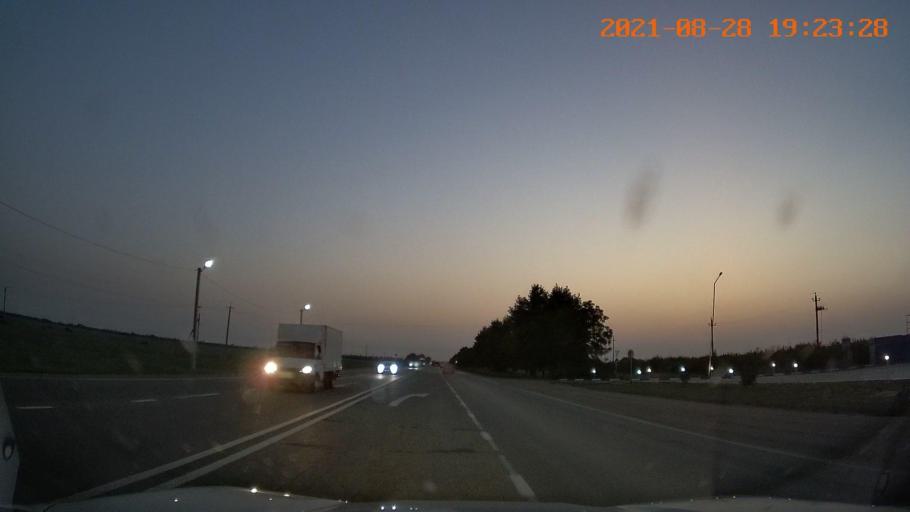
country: RU
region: Adygeya
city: Ponezhukay
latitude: 44.8748
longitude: 39.4499
